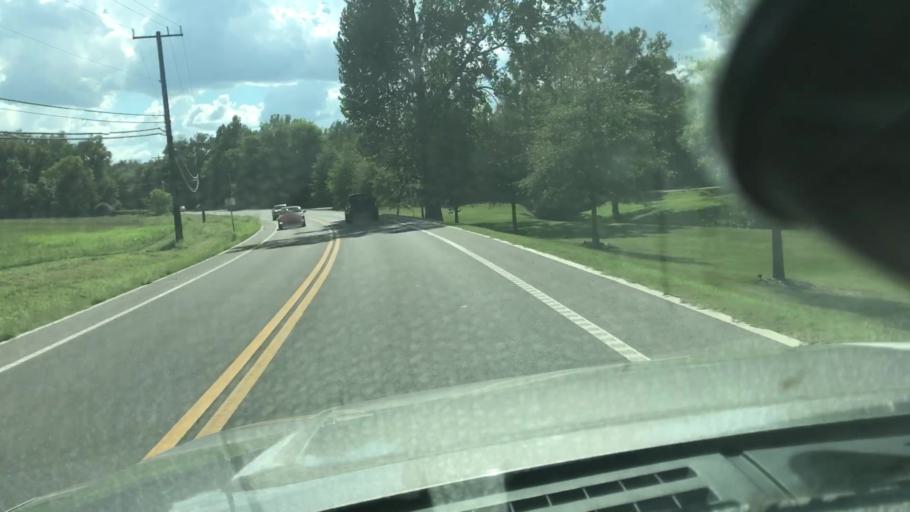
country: US
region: Tennessee
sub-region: Cheatham County
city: Pegram
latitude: 36.0263
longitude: -87.0219
